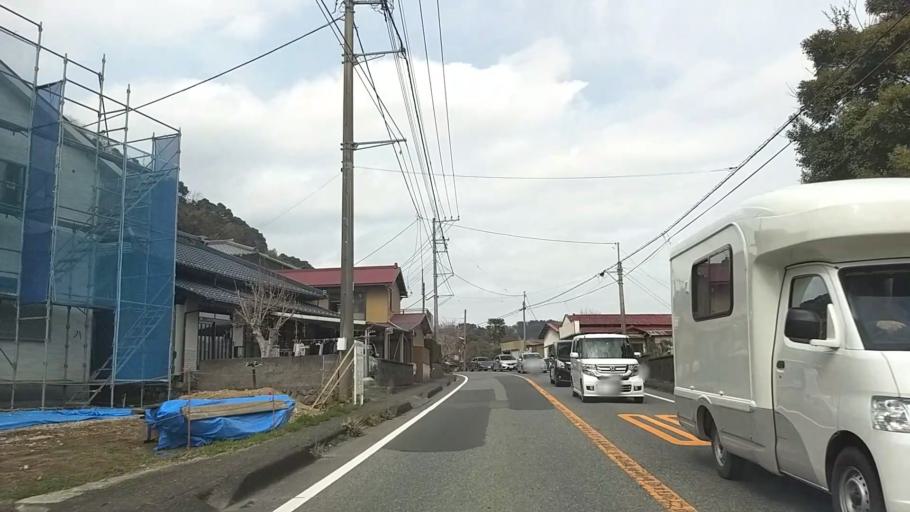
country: JP
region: Shizuoka
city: Heda
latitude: 34.9136
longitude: 138.9241
